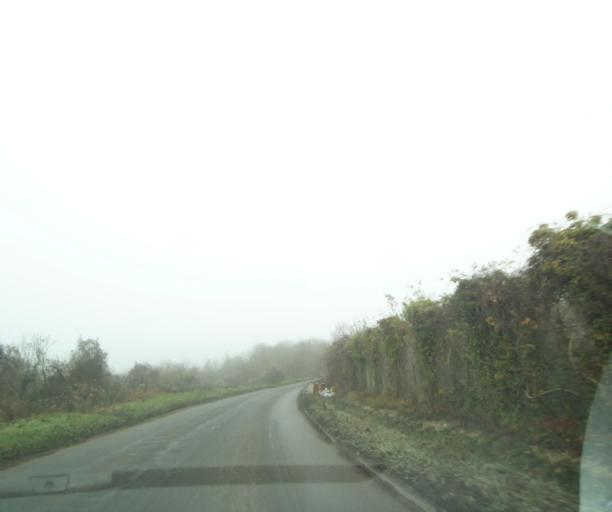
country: FR
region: Ile-de-France
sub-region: Departement de Seine-et-Marne
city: Courtry
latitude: 48.9223
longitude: 2.5952
